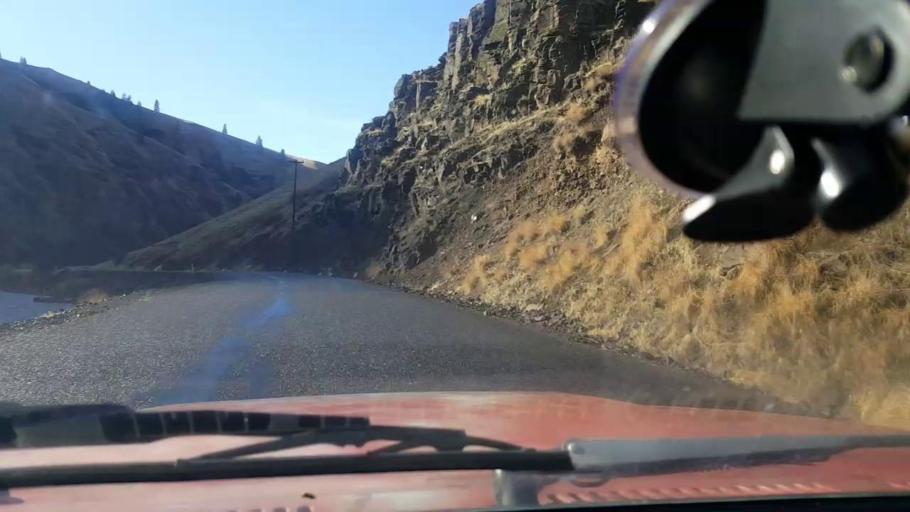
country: US
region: Washington
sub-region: Asotin County
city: Asotin
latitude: 46.0223
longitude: -117.3418
